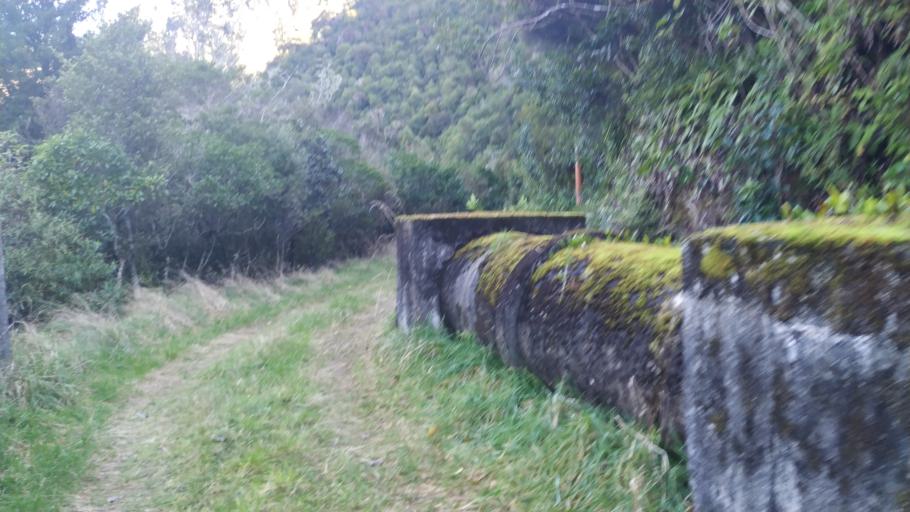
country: NZ
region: Nelson
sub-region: Nelson City
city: Nelson
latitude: -41.2958
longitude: 173.3439
